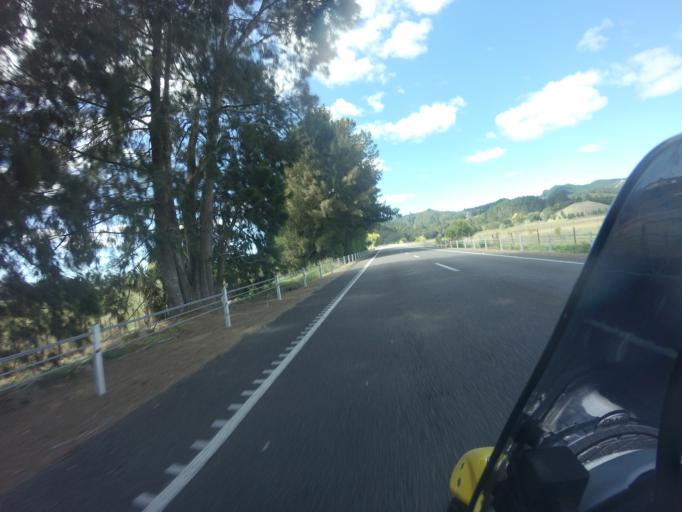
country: NZ
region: Bay of Plenty
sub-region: Whakatane District
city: Edgecumbe
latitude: -38.0224
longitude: 176.8428
